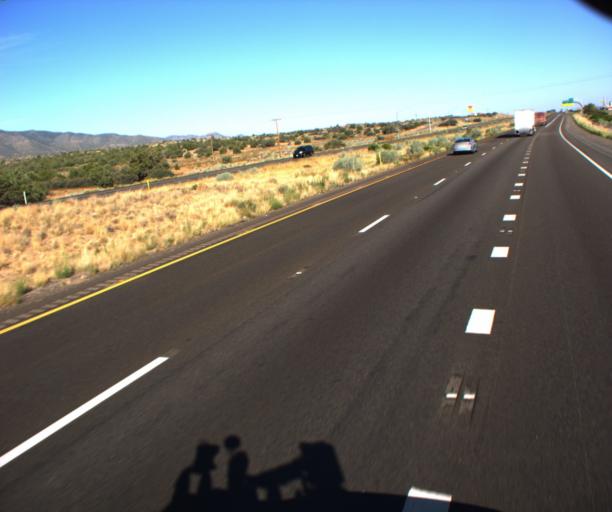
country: US
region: Arizona
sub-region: Mohave County
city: New Kingman-Butler
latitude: 35.1737
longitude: -113.7829
